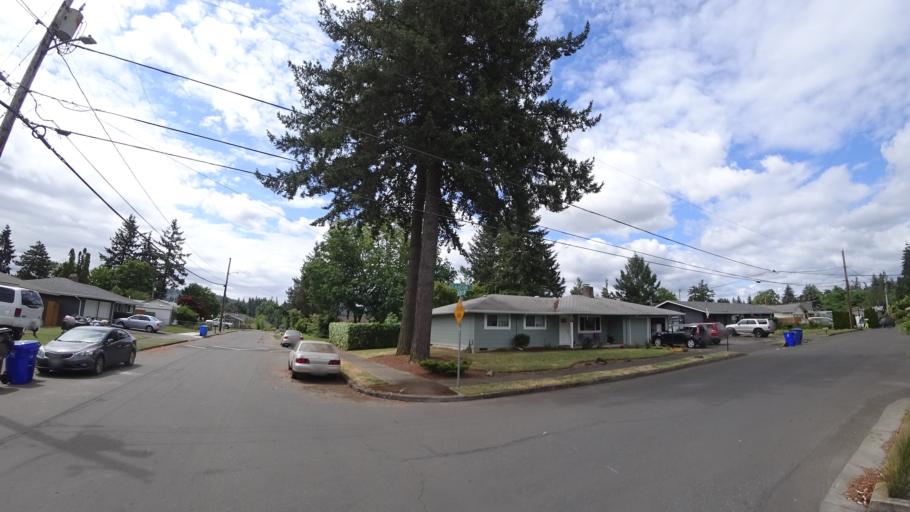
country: US
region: Oregon
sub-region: Multnomah County
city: Lents
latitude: 45.4924
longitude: -122.5276
